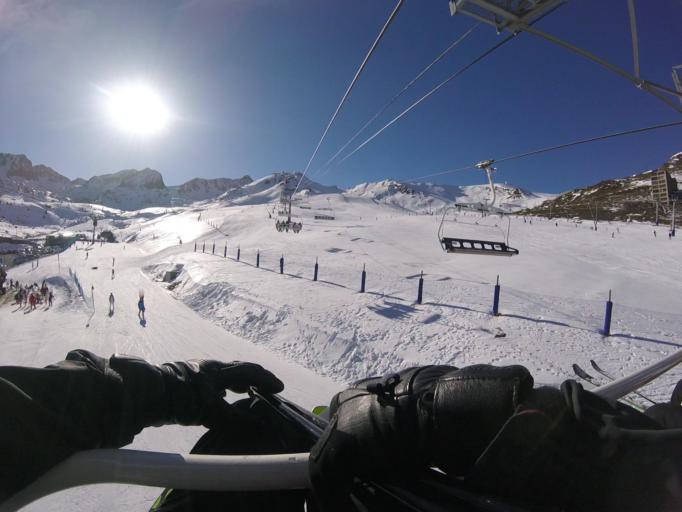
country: AD
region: Encamp
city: Pas de la Casa
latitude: 42.5393
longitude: 1.7332
